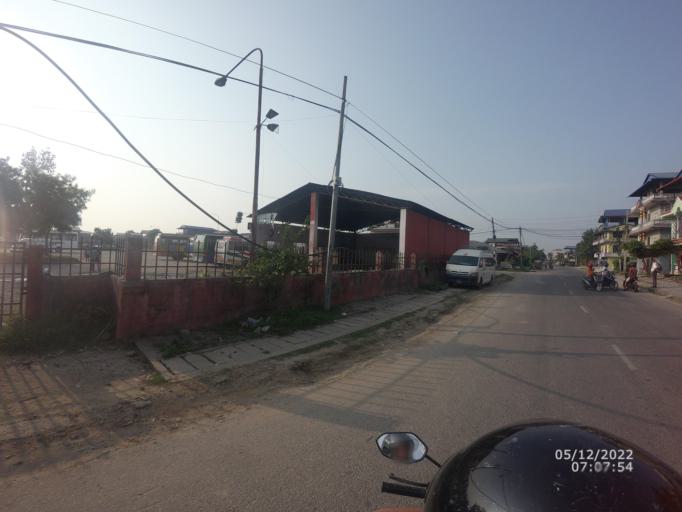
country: NP
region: Central Region
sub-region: Narayani Zone
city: Bharatpur
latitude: 27.6669
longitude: 84.4382
